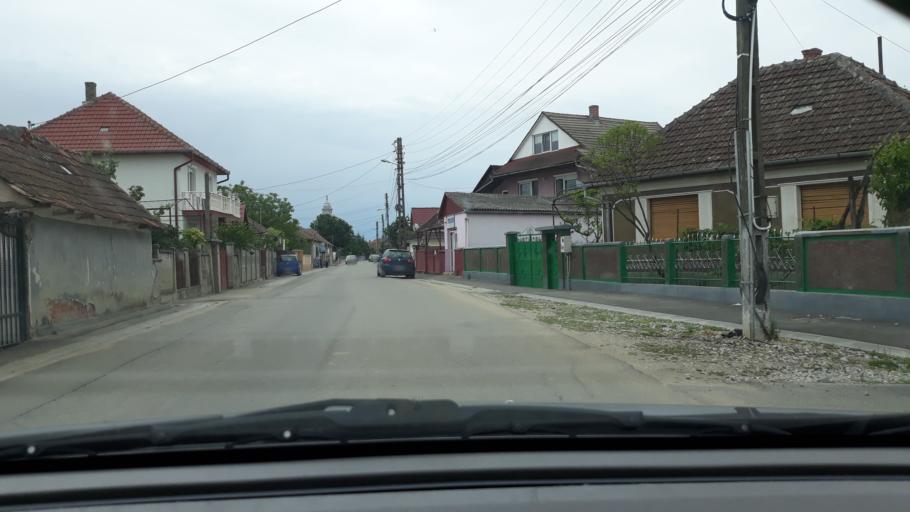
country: RO
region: Bihor
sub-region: Comuna Osorheiu
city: Osorheiu
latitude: 47.0585
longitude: 22.0435
